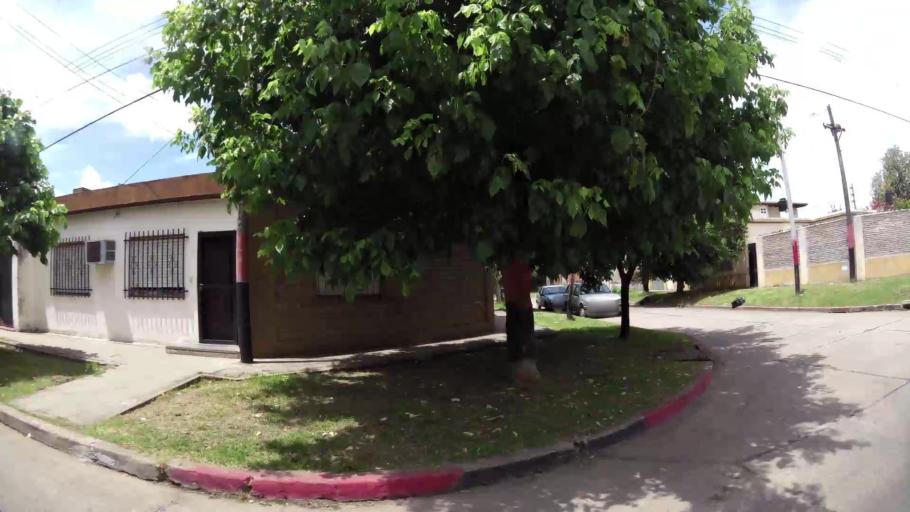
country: AR
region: Santa Fe
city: Gobernador Galvez
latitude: -32.9996
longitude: -60.6221
